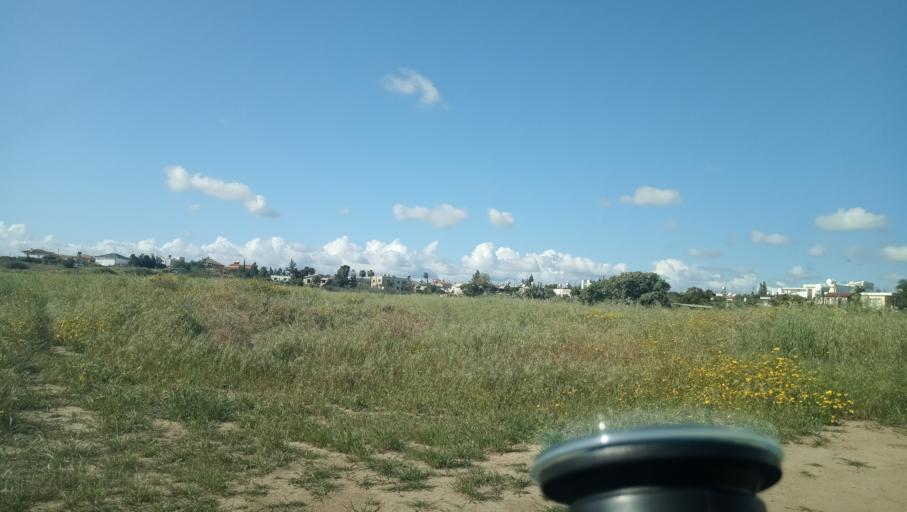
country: CY
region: Lefkosia
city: Geri
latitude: 35.1027
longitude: 33.3949
